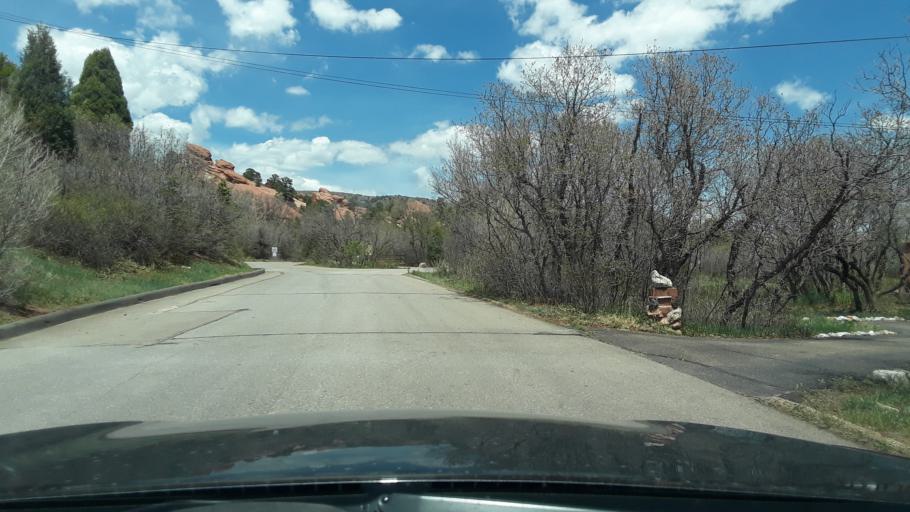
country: US
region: Colorado
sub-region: El Paso County
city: Manitou Springs
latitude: 38.8661
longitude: -104.8848
